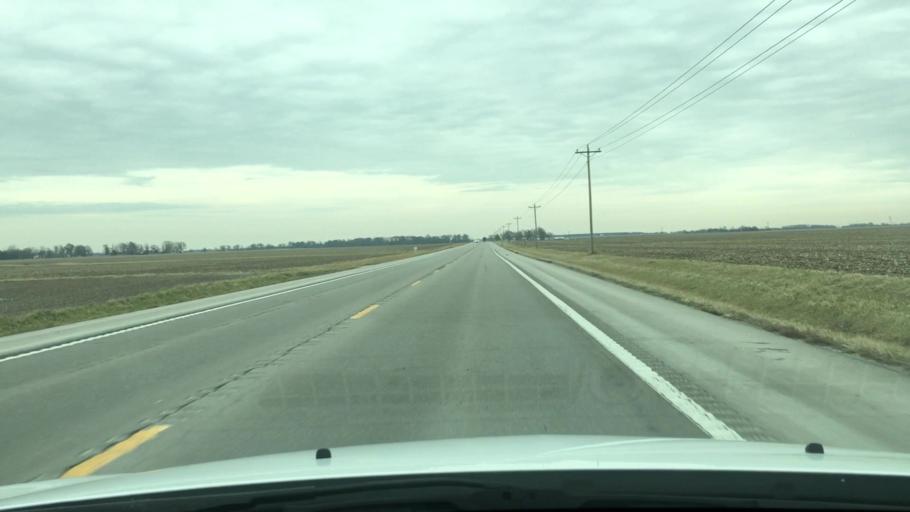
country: US
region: Missouri
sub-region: Audrain County
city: Mexico
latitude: 39.1639
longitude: -91.7772
